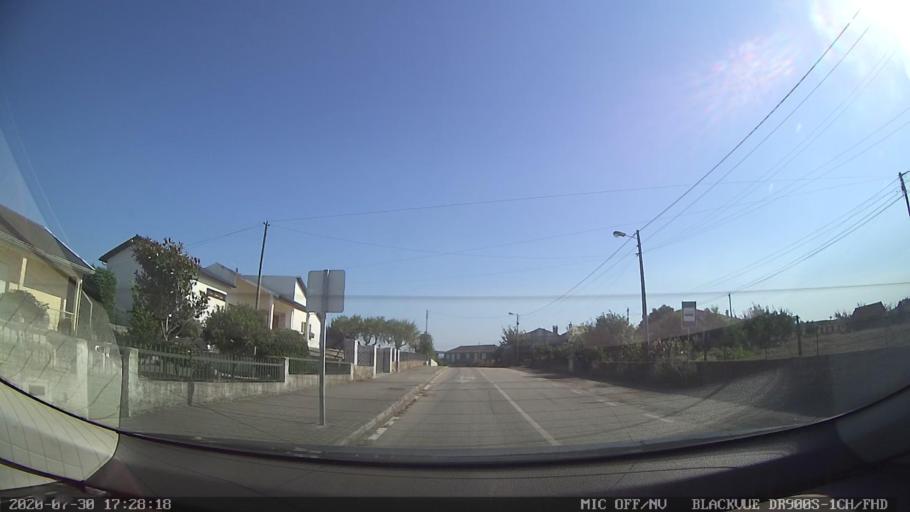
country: PT
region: Vila Real
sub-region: Murca
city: Murca
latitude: 41.3283
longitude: -7.4661
